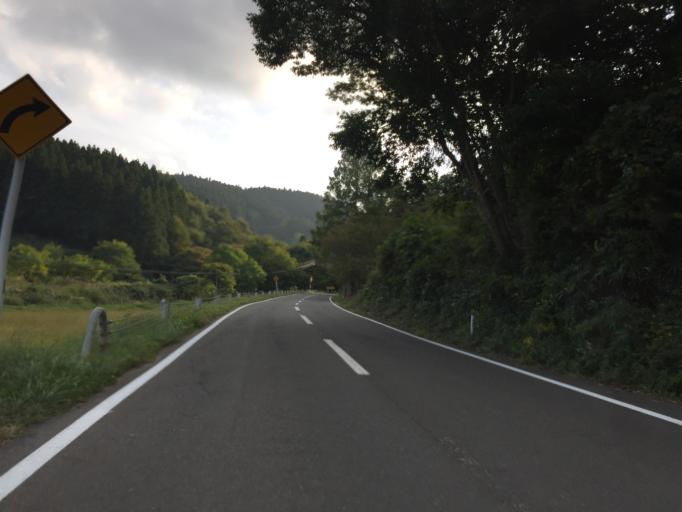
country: JP
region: Fukushima
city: Funehikimachi-funehiki
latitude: 37.5843
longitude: 140.6987
